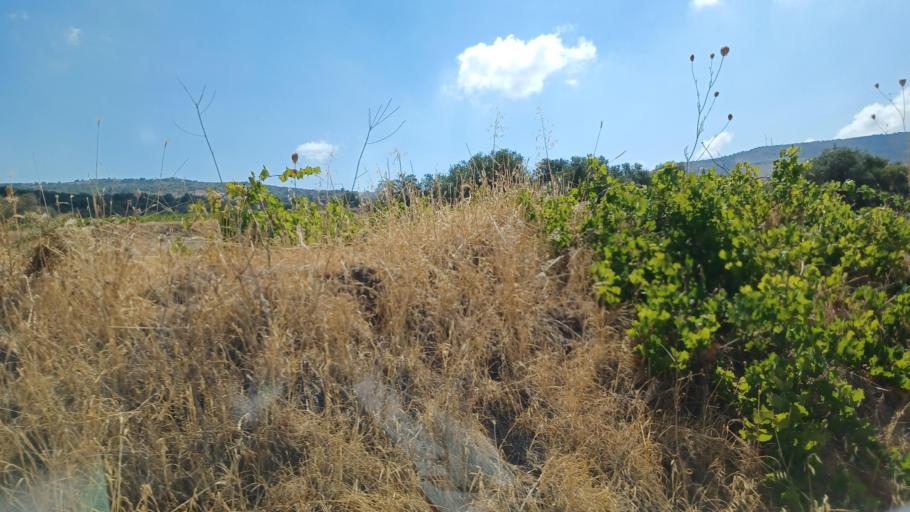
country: CY
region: Pafos
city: Mesogi
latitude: 34.8728
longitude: 32.5984
